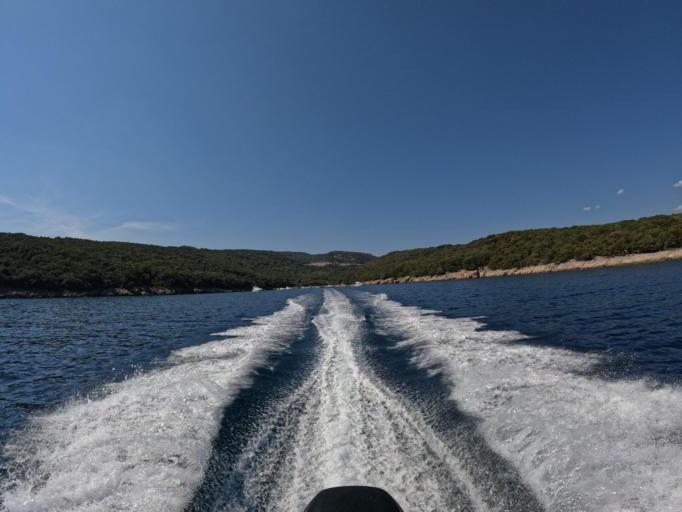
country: HR
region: Primorsko-Goranska
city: Cres
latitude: 44.9484
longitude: 14.4646
